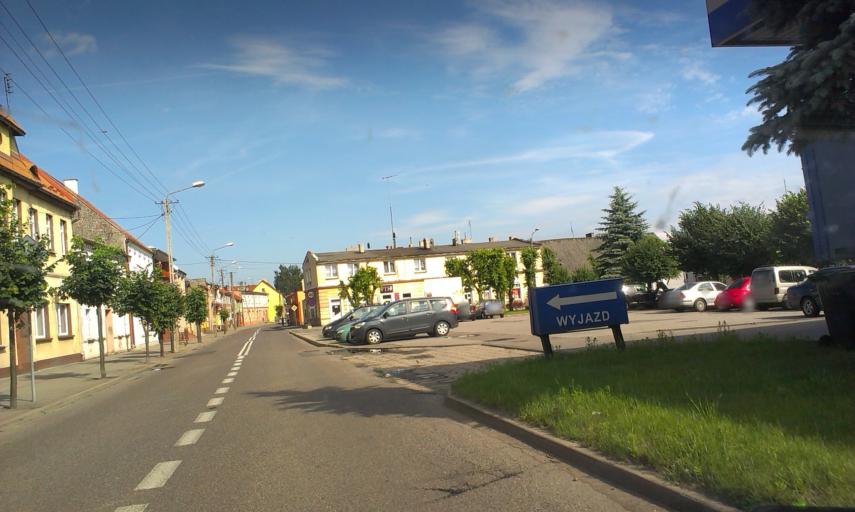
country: PL
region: Greater Poland Voivodeship
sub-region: Powiat pilski
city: Wysoka
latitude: 53.1818
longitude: 17.0801
